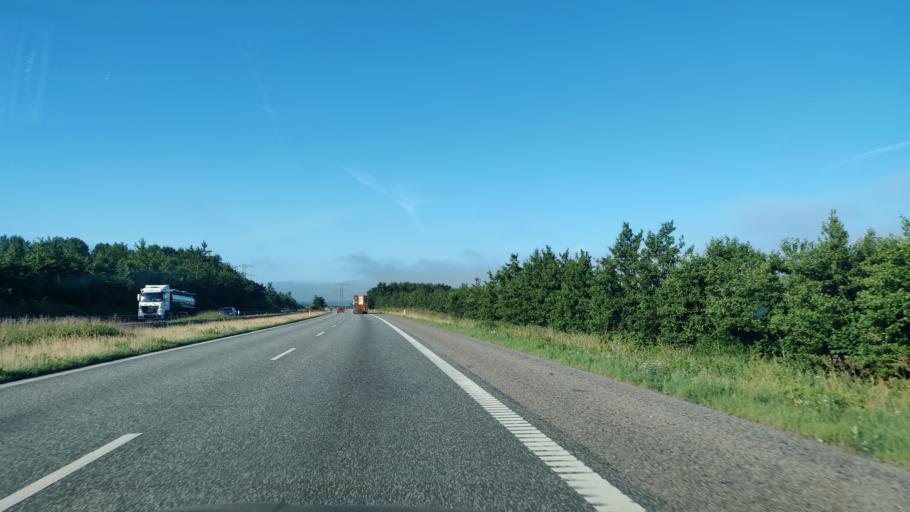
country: DK
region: North Denmark
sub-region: Rebild Kommune
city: Stovring
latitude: 56.8349
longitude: 9.7316
